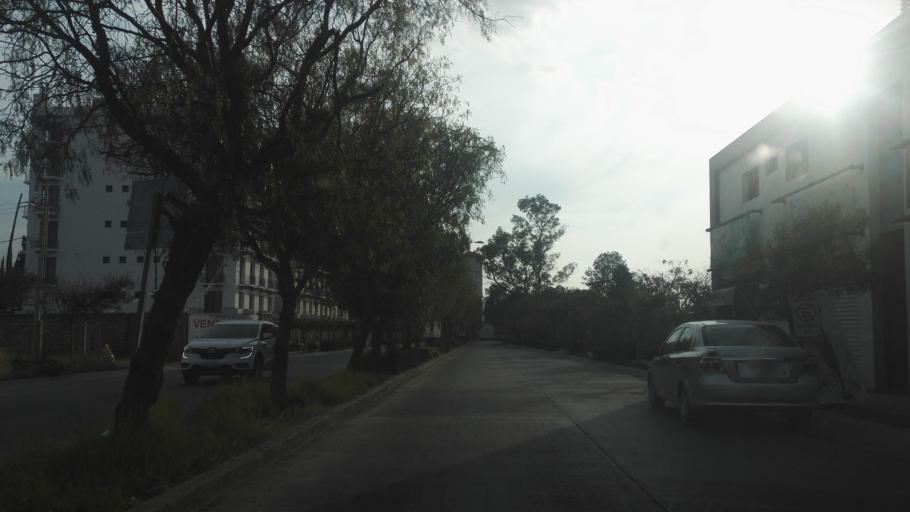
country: MX
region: Guanajuato
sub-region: Leon
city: Ladrilleras del Refugio
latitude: 21.0686
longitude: -101.5951
